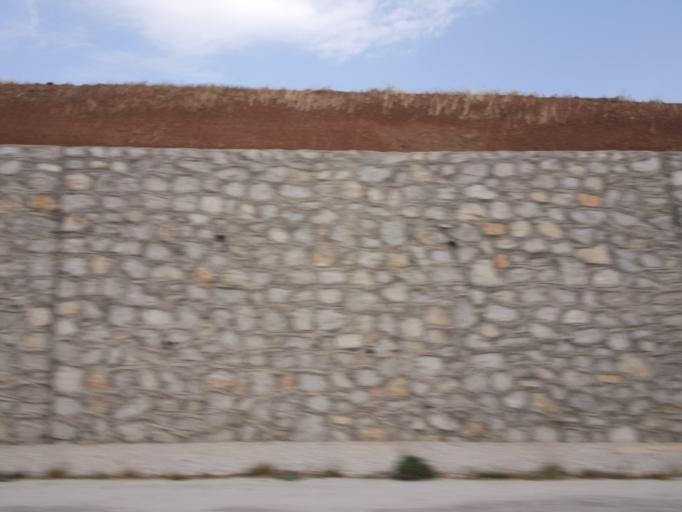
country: TR
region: Corum
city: Alaca
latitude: 40.1486
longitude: 34.7675
